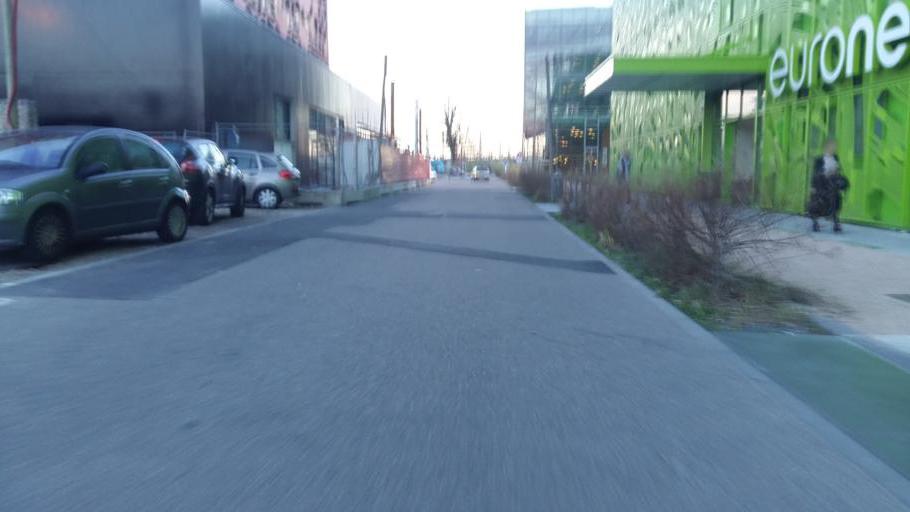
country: FR
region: Rhone-Alpes
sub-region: Departement du Rhone
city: La Mulatiere
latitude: 45.7348
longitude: 4.8158
